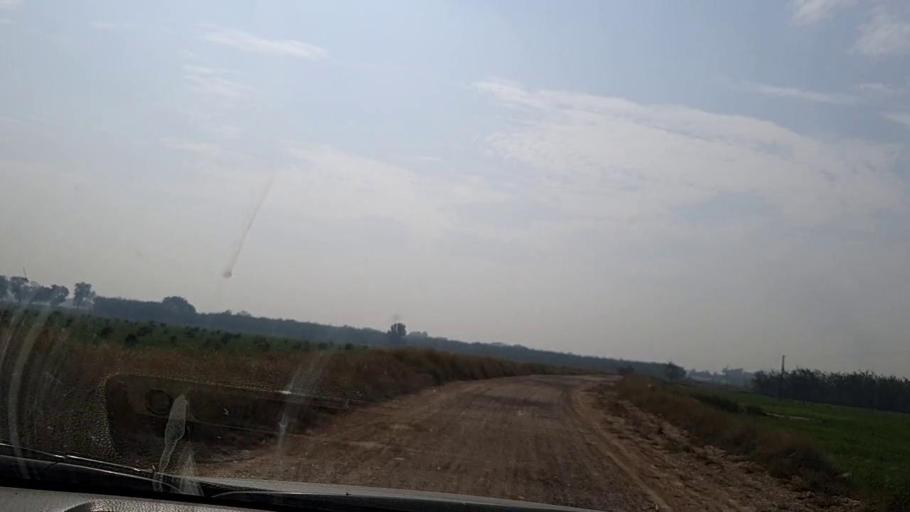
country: PK
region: Sindh
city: Daulatpur
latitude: 26.5319
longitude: 67.9823
